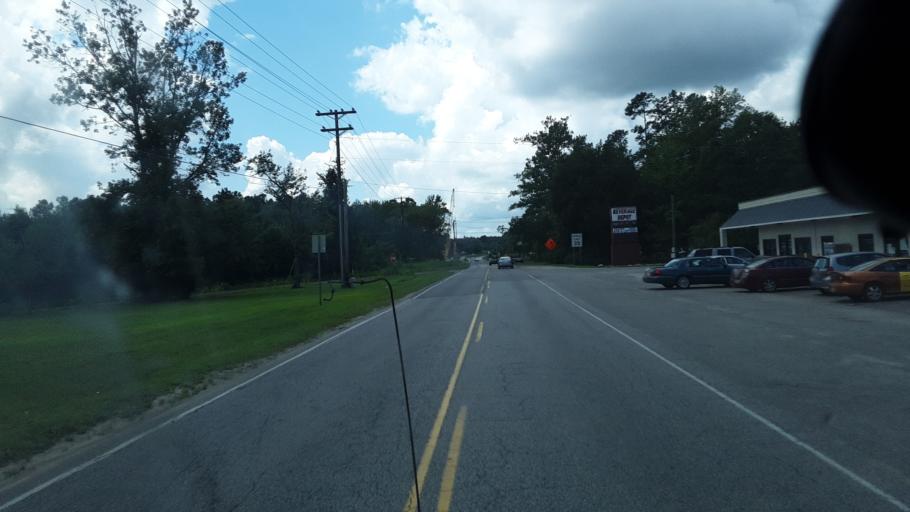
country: US
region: South Carolina
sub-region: Williamsburg County
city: Andrews
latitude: 33.3733
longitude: -79.4473
